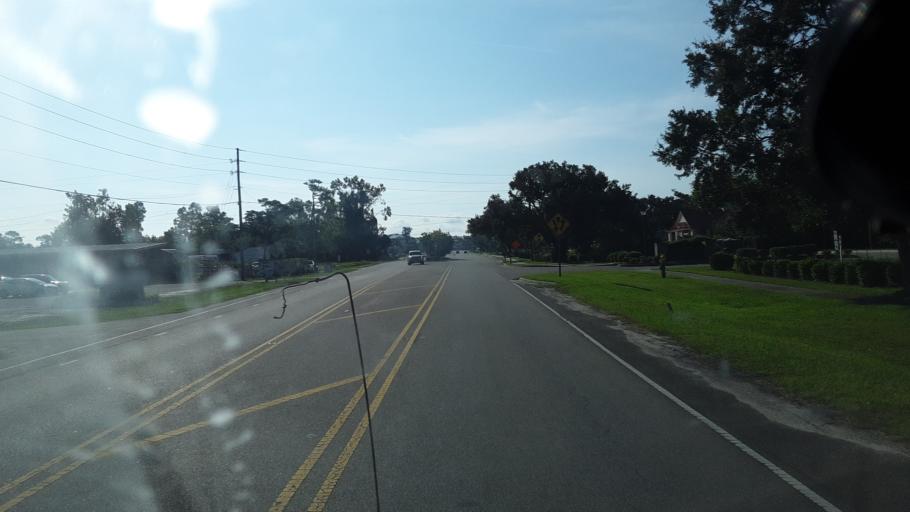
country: US
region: North Carolina
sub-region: Brunswick County
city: Navassa
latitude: 34.2383
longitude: -78.0070
